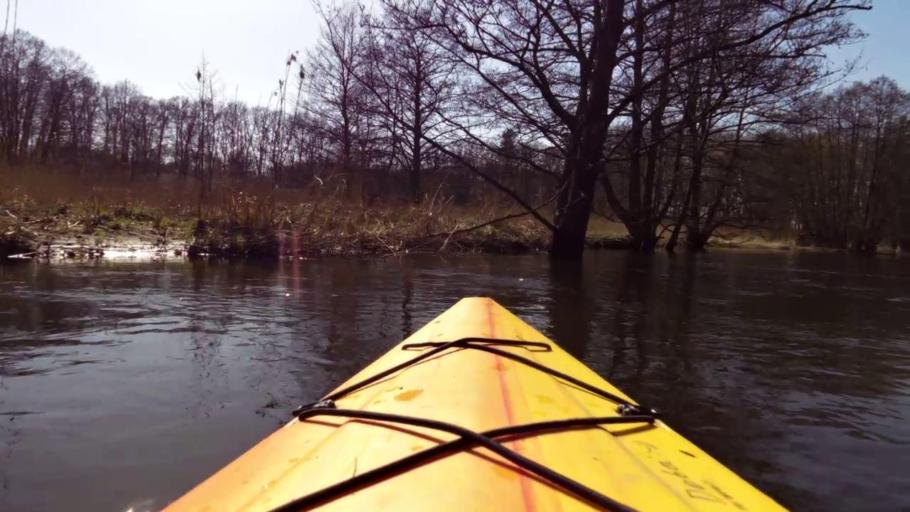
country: PL
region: West Pomeranian Voivodeship
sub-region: Powiat lobeski
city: Resko
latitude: 53.7599
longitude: 15.4790
